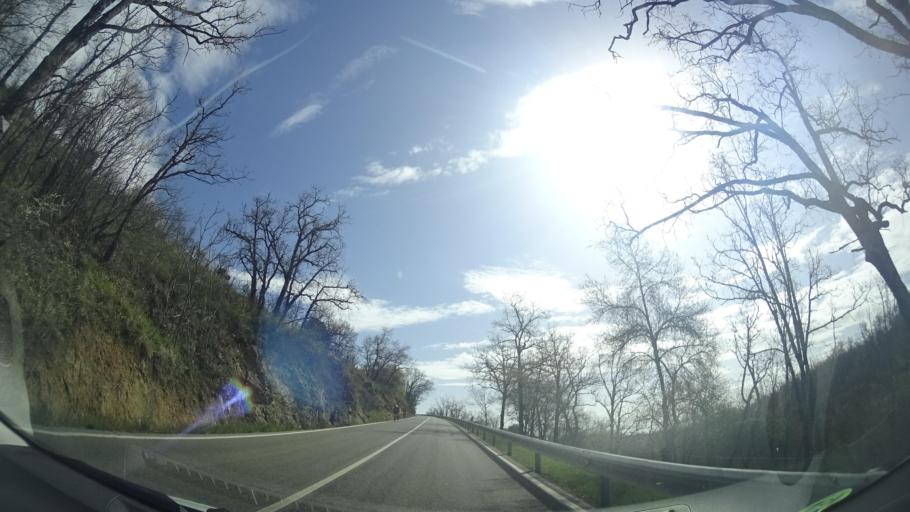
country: ES
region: Madrid
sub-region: Provincia de Madrid
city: Miraflores de la Sierra
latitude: 40.7889
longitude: -3.7767
